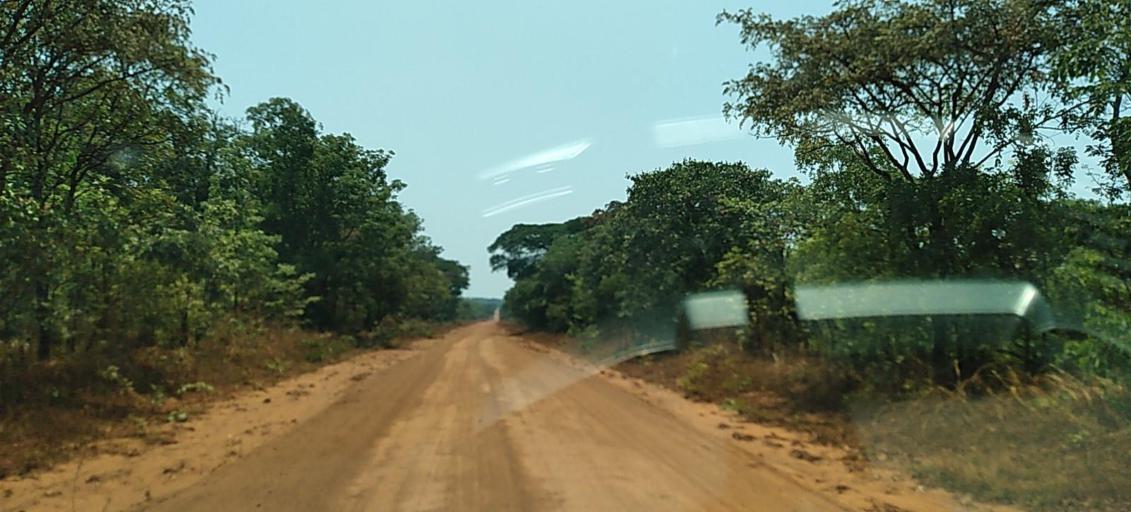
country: ZM
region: North-Western
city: Kansanshi
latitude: -11.9887
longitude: 26.8440
